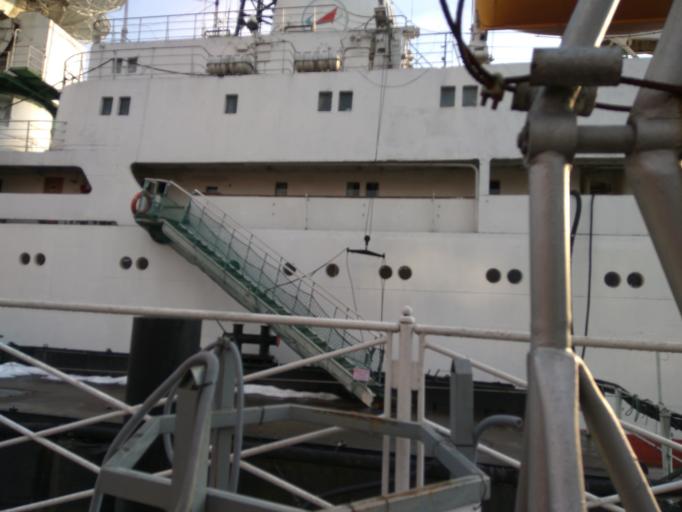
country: RU
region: Kaliningrad
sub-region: Gorod Kaliningrad
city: Kaliningrad
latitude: 54.7065
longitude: 20.4971
